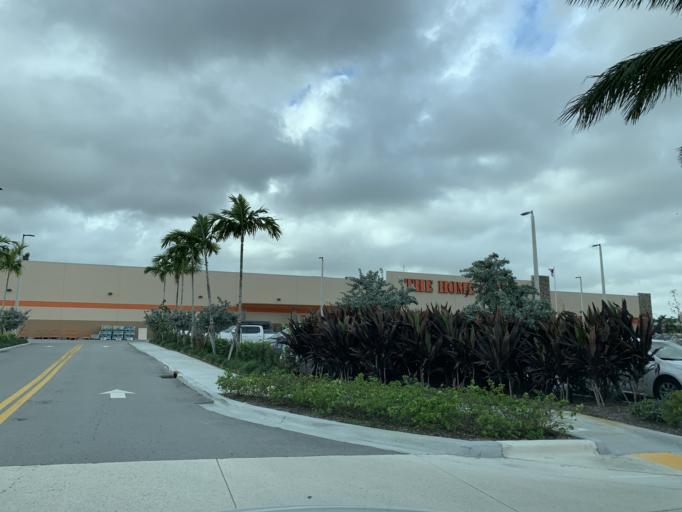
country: US
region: Florida
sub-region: Miami-Dade County
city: Sweetwater
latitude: 25.7883
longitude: -80.3872
